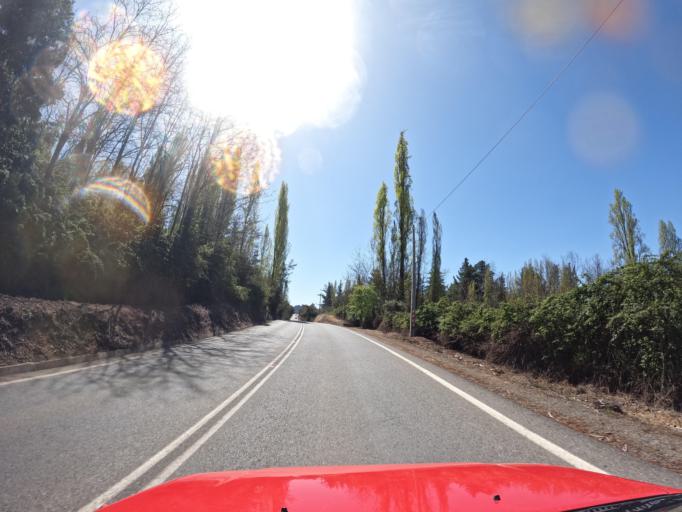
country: CL
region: Maule
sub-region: Provincia de Talca
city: San Clemente
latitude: -35.4557
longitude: -71.2690
